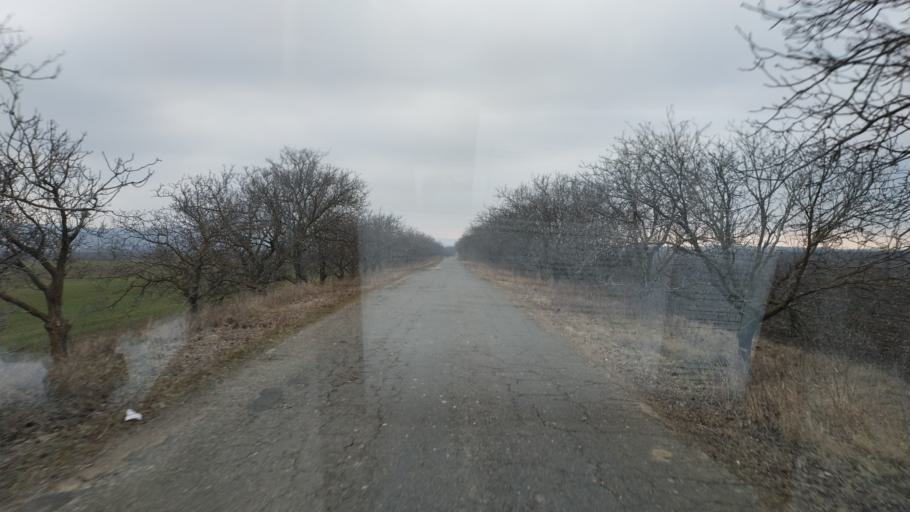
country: MD
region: Hincesti
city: Dancu
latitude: 46.8876
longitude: 28.3008
